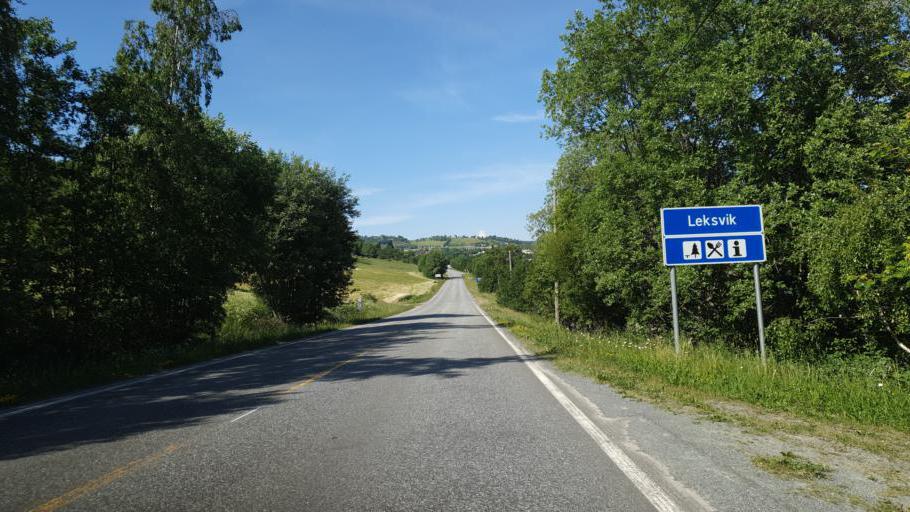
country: NO
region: Nord-Trondelag
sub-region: Leksvik
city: Leksvik
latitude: 63.6598
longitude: 10.6085
